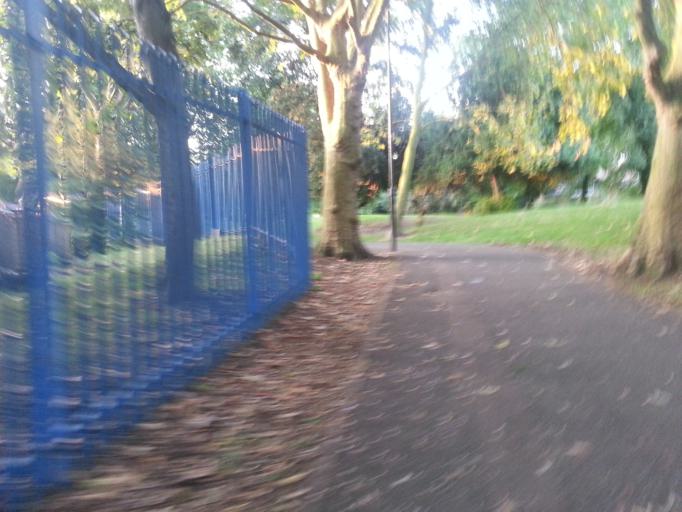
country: GB
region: England
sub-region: Greater London
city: Harringay
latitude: 51.5866
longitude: -0.0884
